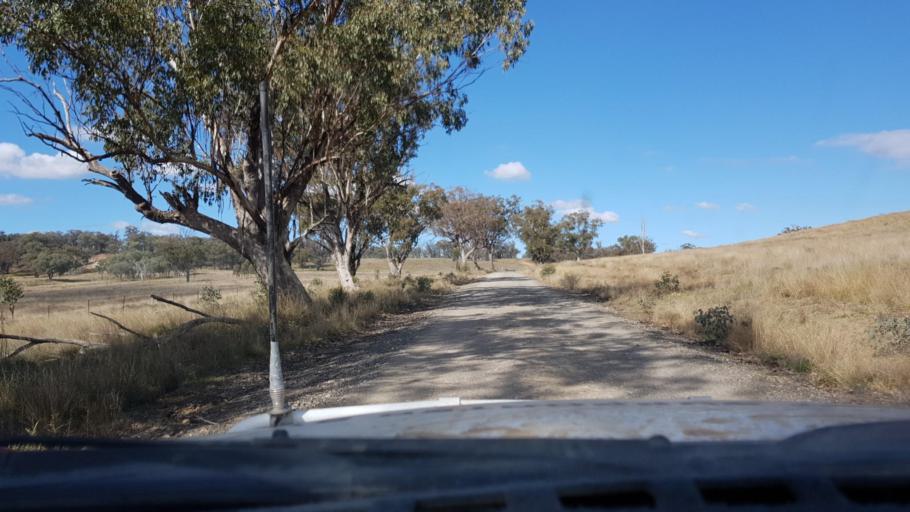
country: AU
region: New South Wales
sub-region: Tamworth Municipality
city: Manilla
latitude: -30.4589
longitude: 150.7425
